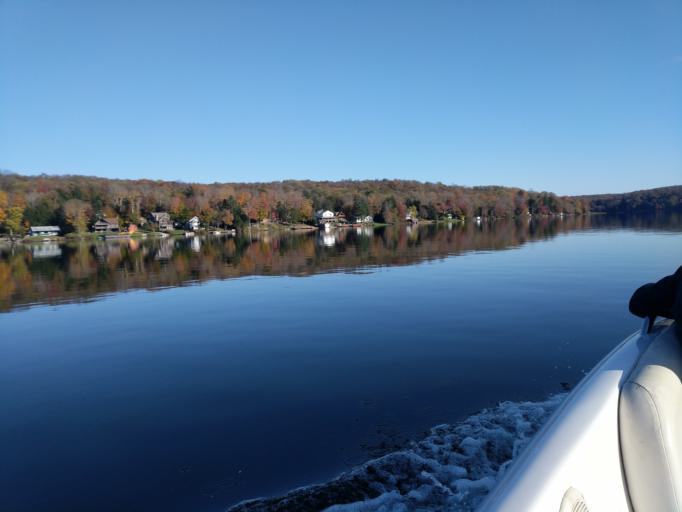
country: US
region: New York
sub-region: Sullivan County
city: Livingston Manor
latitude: 41.8904
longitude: -74.9802
